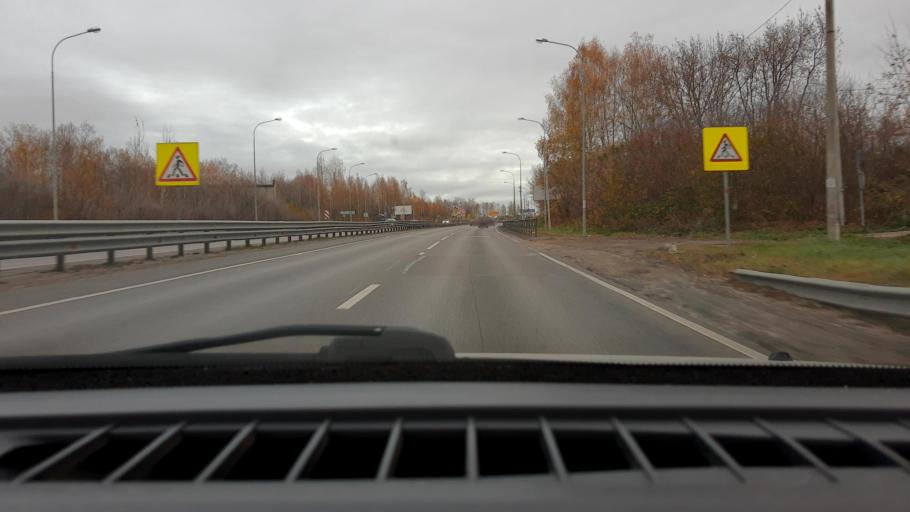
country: RU
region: Nizjnij Novgorod
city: Afonino
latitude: 56.2339
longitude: 44.0613
